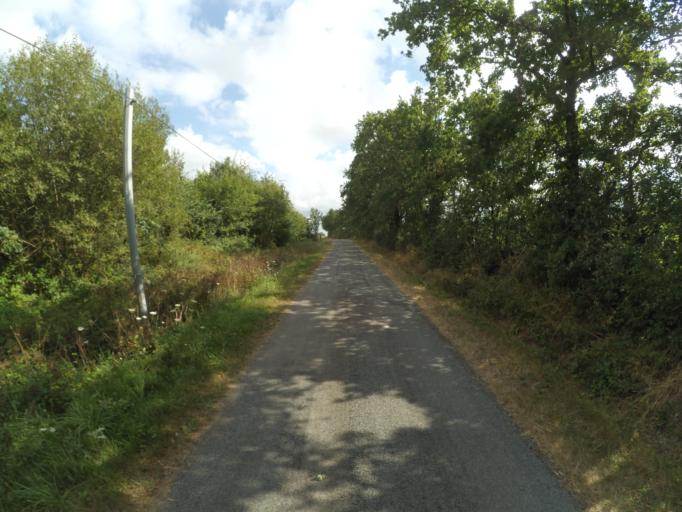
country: FR
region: Pays de la Loire
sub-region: Departement de la Loire-Atlantique
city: Vieillevigne
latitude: 46.9945
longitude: -1.4675
